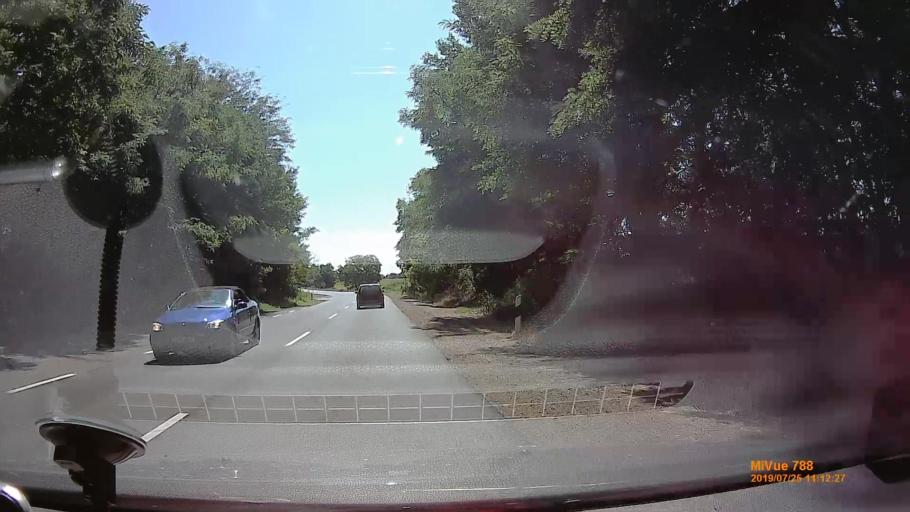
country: HU
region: Szabolcs-Szatmar-Bereg
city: Nagykallo
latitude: 47.9002
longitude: 21.7919
